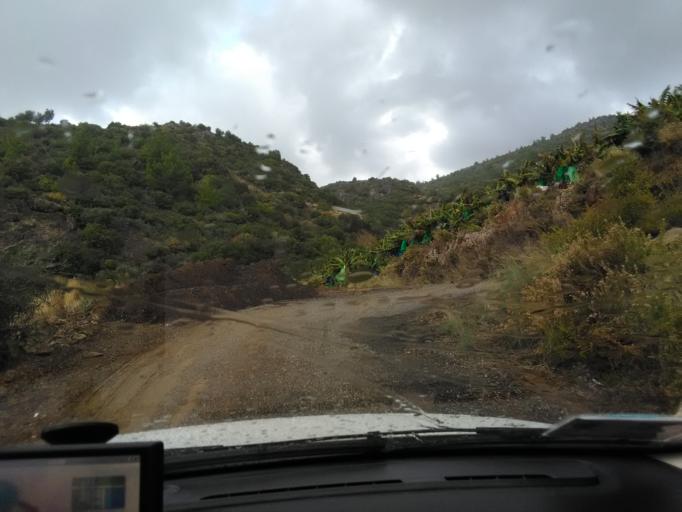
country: TR
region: Antalya
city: Gazipasa
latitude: 36.1614
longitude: 32.4219
